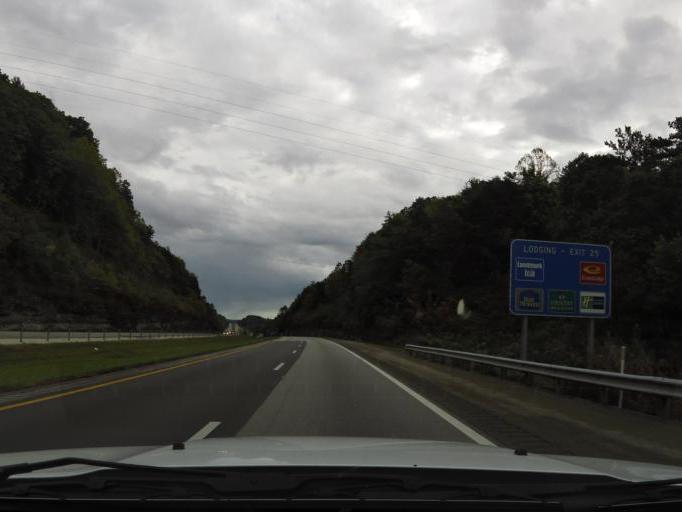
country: US
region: Kentucky
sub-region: Whitley County
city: Corbin
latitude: 36.9035
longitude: -84.1332
